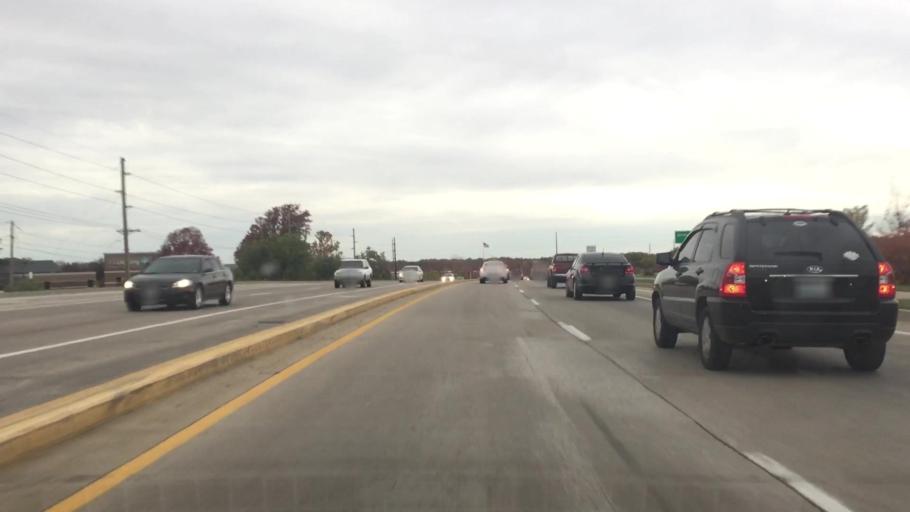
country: US
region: Missouri
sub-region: Boone County
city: Columbia
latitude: 38.9134
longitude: -92.3139
